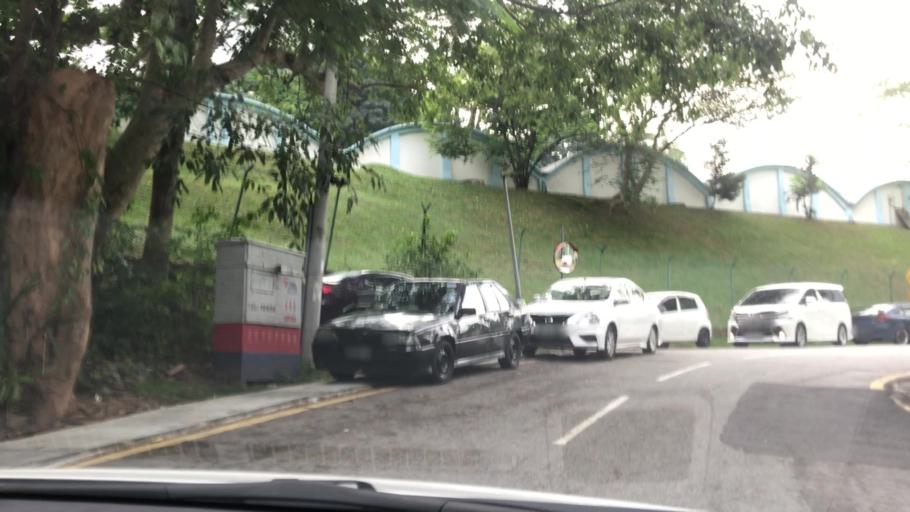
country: MY
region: Kuala Lumpur
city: Kuala Lumpur
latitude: 3.1526
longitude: 101.7051
